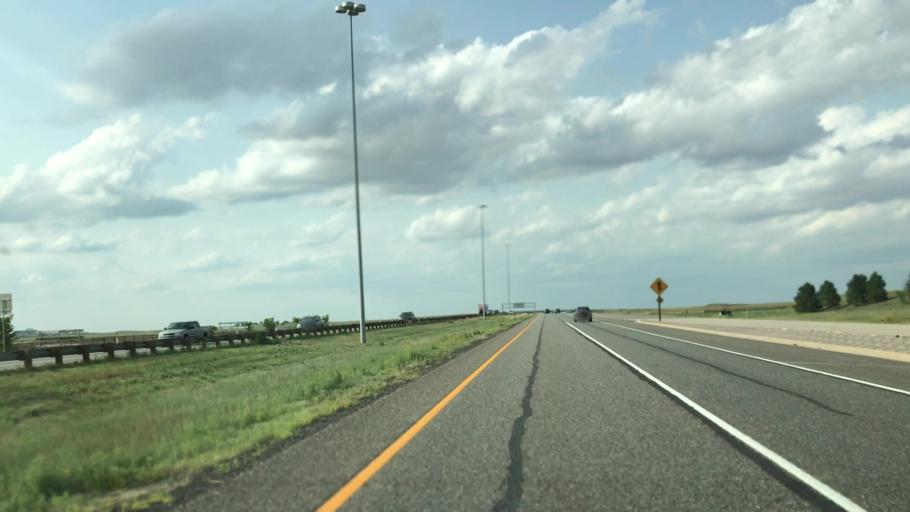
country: US
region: Colorado
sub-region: Adams County
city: Aurora
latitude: 39.7719
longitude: -104.7164
